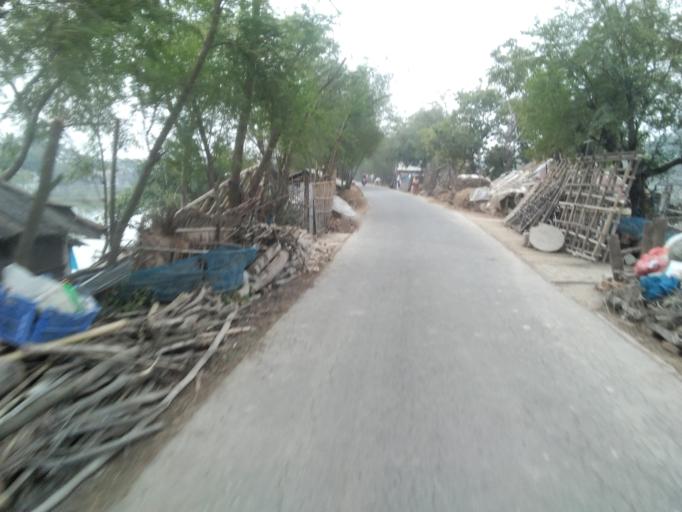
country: BD
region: Khulna
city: Satkhira
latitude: 22.5827
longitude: 89.0672
